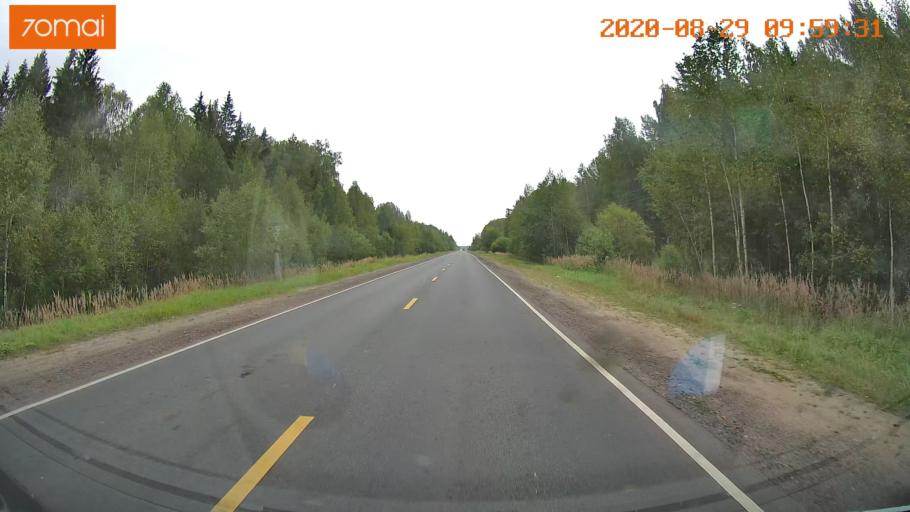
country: RU
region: Ivanovo
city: Zarechnyy
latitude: 57.4110
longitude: 42.3683
